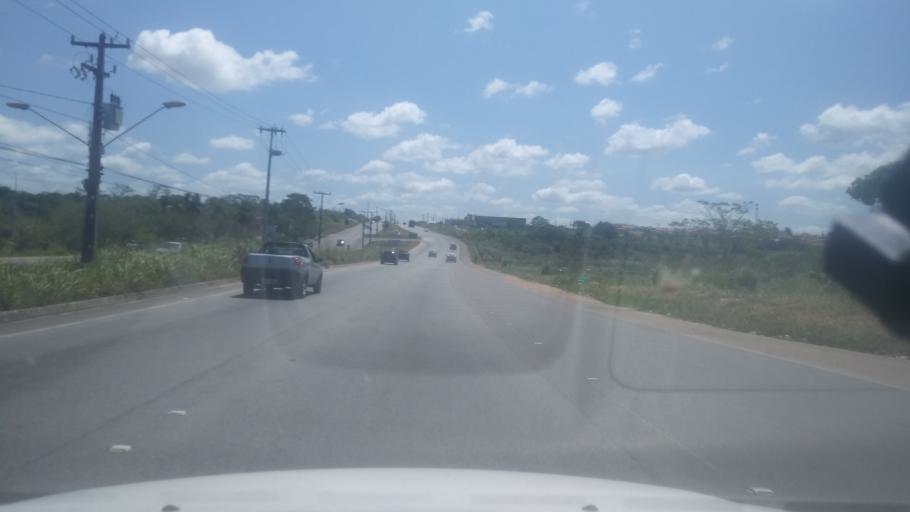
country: BR
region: Rio Grande do Norte
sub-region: Sao Goncalo Do Amarante
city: Sao Goncalo do Amarante
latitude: -5.7583
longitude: -35.3001
